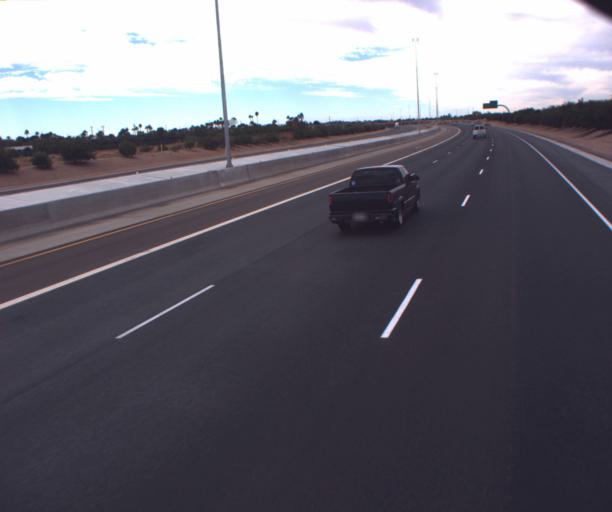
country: US
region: Arizona
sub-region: Maricopa County
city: Mesa
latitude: 33.4767
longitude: -111.7766
